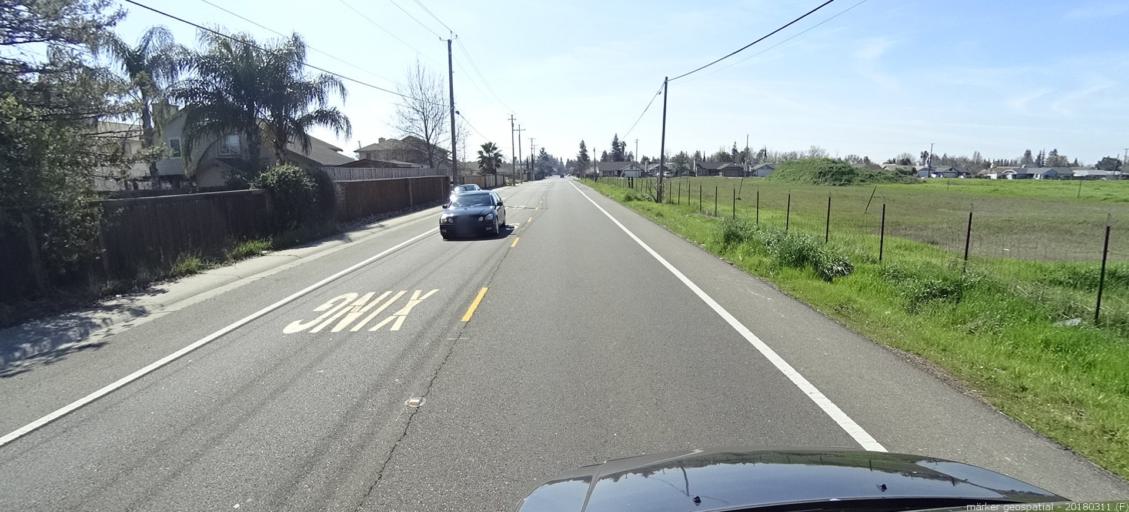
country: US
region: California
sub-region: Sacramento County
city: Florin
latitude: 38.4668
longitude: -121.3903
